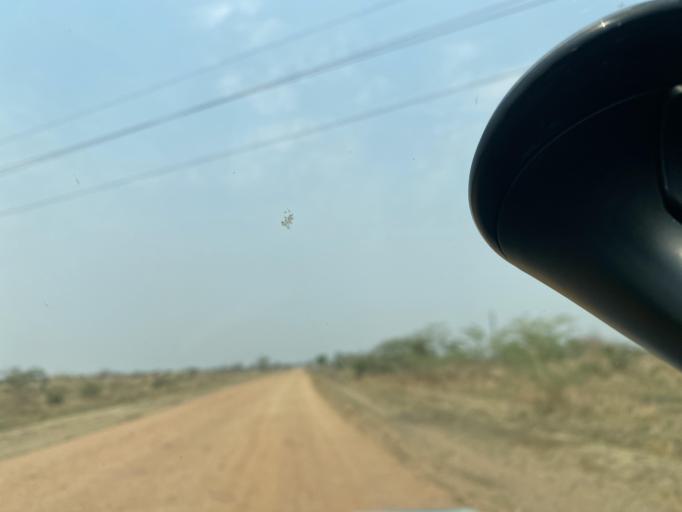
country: ZM
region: Lusaka
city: Kafue
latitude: -15.6774
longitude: 28.0141
